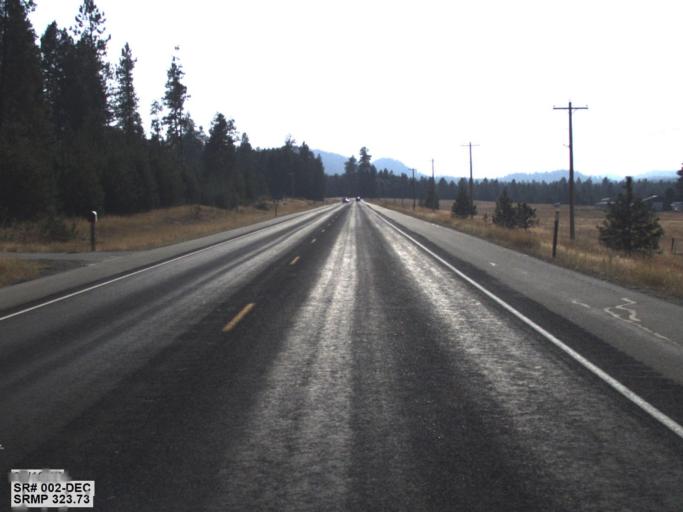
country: US
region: Washington
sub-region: Pend Oreille County
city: Newport
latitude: 48.1086
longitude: -117.2327
